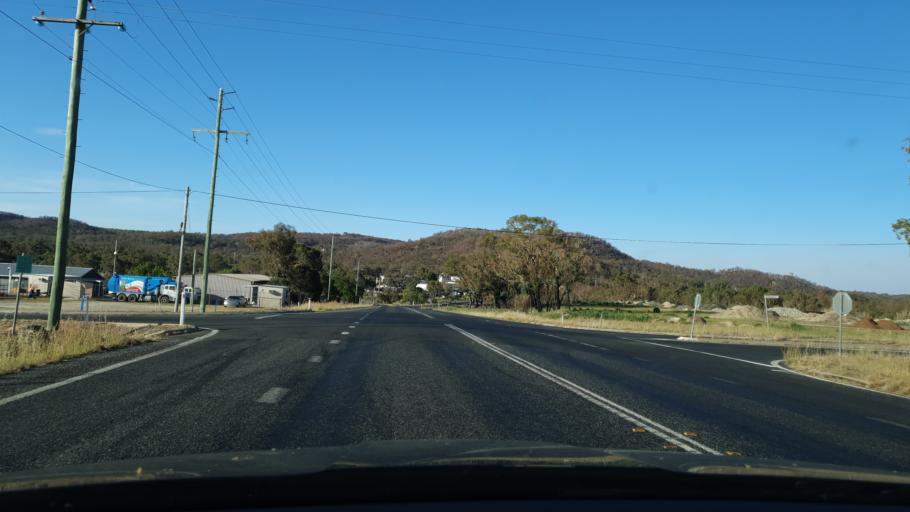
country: AU
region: Queensland
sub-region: Southern Downs
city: Stanthorpe
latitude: -28.6568
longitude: 151.9172
